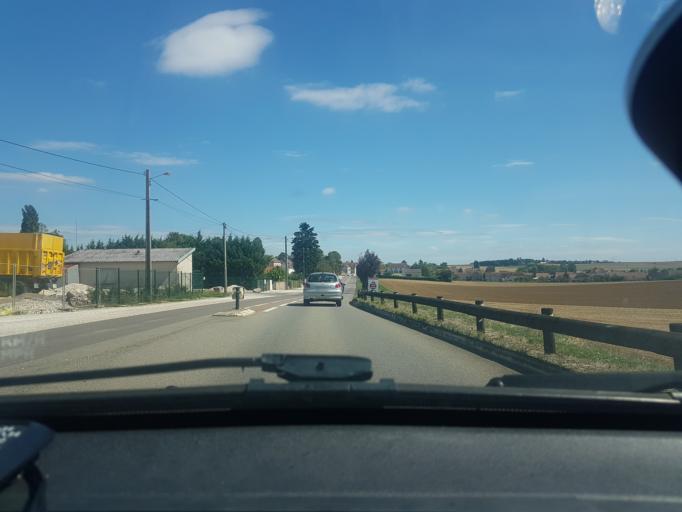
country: FR
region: Bourgogne
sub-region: Departement de la Cote-d'Or
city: Belleneuve
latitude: 47.3801
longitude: 5.2461
